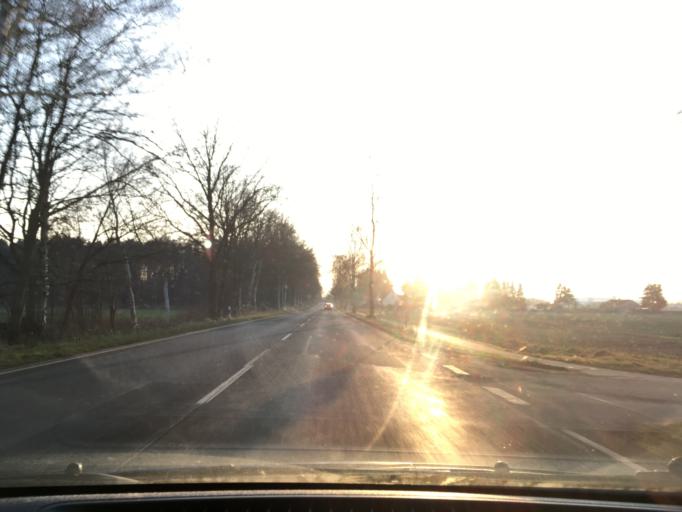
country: DE
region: Lower Saxony
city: Eschede
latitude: 52.7446
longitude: 10.2472
